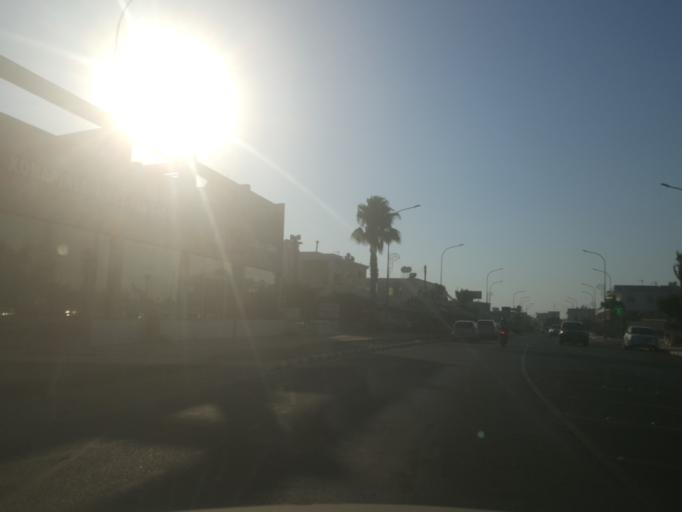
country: CY
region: Ammochostos
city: Deryneia
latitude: 35.0580
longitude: 33.9681
